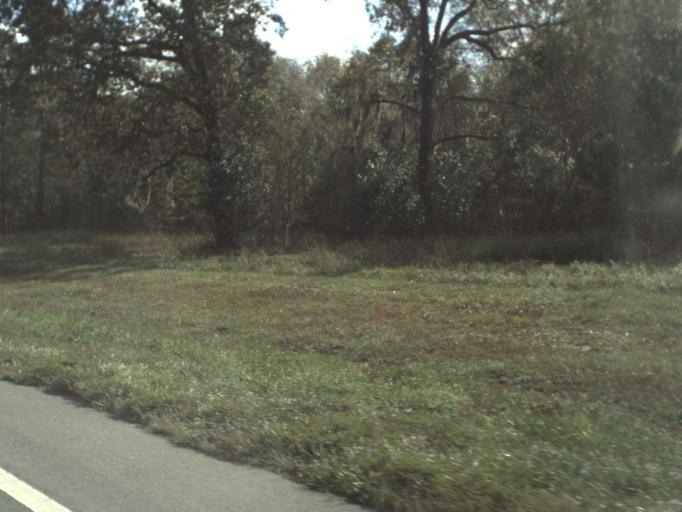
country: US
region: Florida
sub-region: Gadsden County
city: Gretna
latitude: 30.6810
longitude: -84.7114
